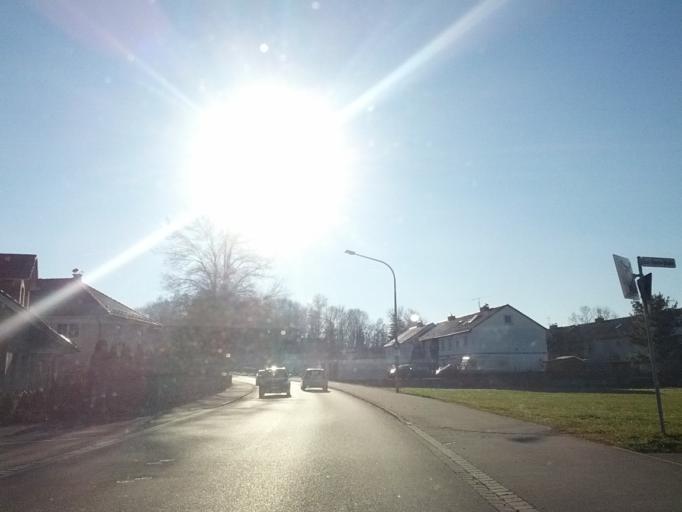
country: DE
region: Bavaria
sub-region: Swabia
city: Buxheim
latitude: 47.9978
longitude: 10.1345
